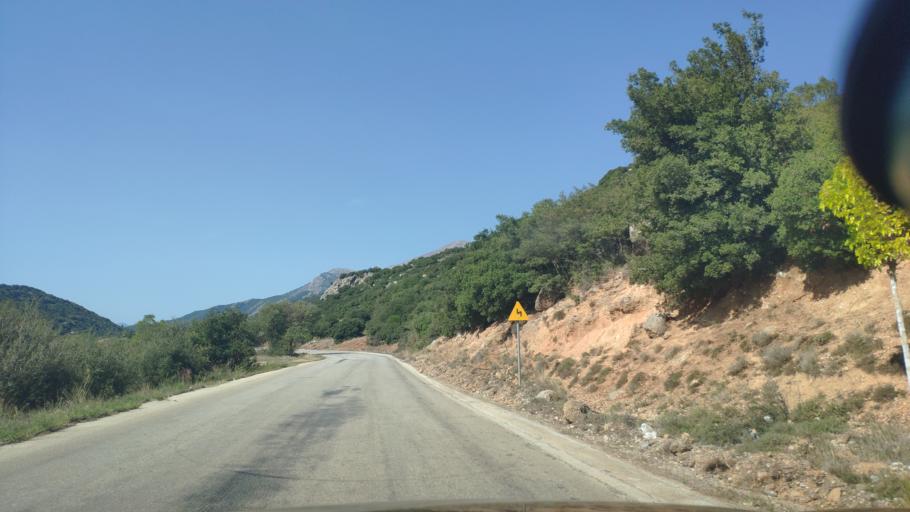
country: GR
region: Peloponnese
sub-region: Nomos Korinthias
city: Nemea
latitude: 37.8896
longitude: 22.5082
